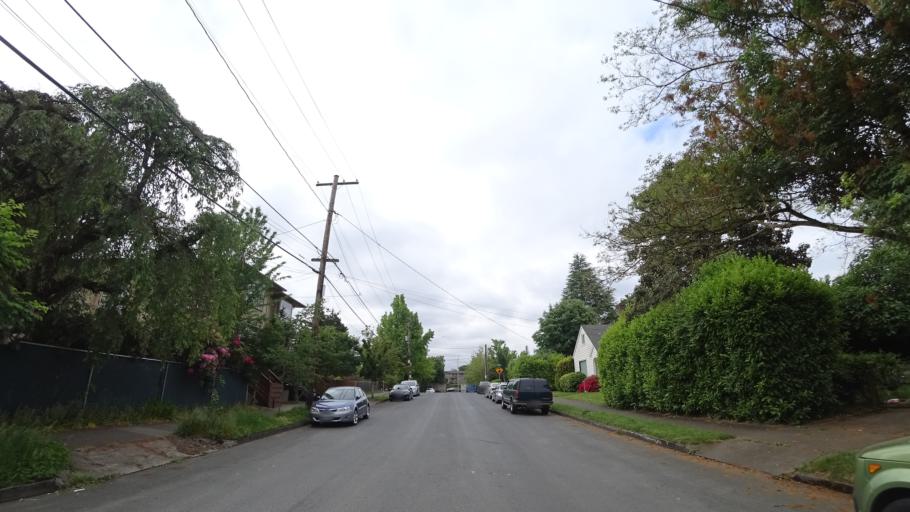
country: US
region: Oregon
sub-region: Clackamas County
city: Milwaukie
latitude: 45.4981
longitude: -122.6263
